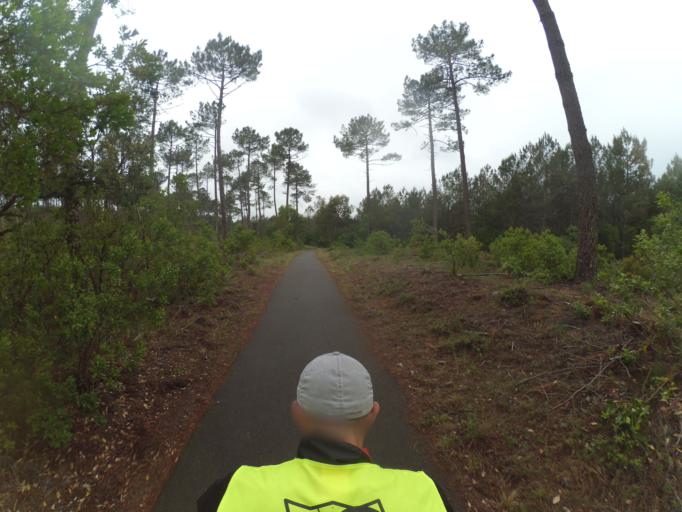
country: FR
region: Aquitaine
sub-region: Departement des Landes
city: Mimizan
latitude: 44.2215
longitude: -1.2529
